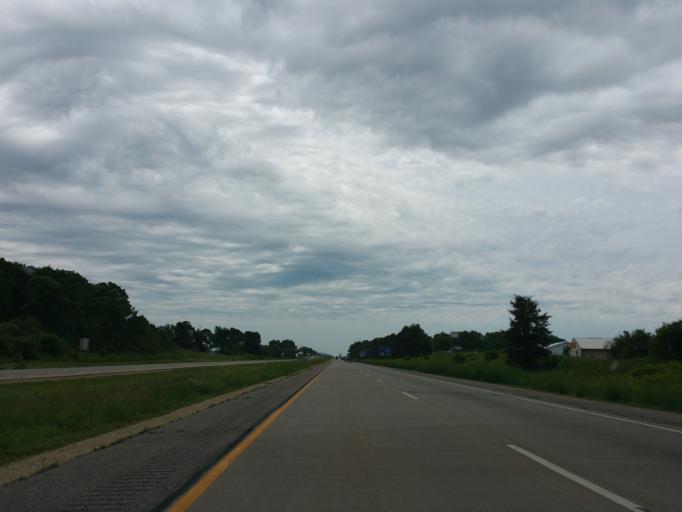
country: US
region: Wisconsin
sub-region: Juneau County
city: Mauston
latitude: 43.8100
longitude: -90.0703
